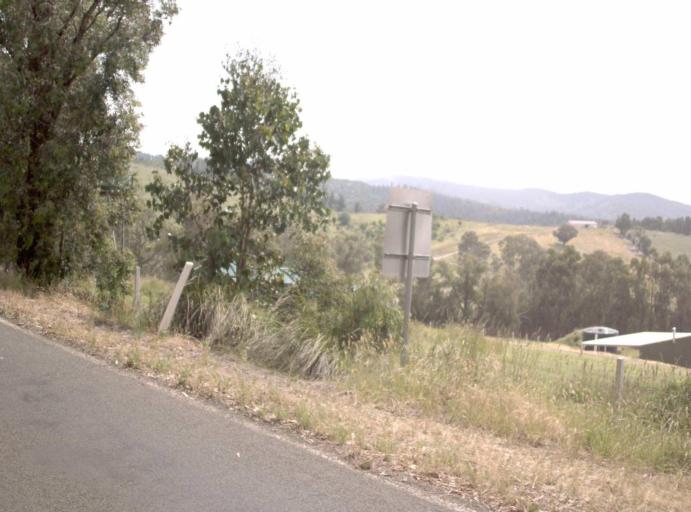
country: AU
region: Victoria
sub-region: Latrobe
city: Traralgon
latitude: -38.3207
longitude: 146.5694
